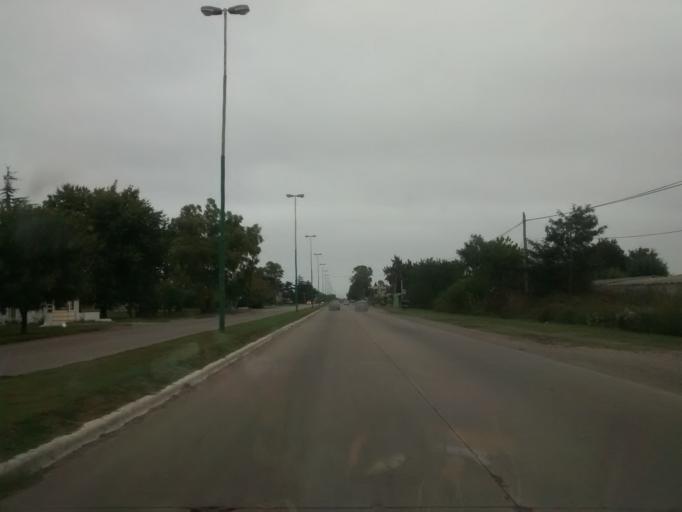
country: AR
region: Buenos Aires
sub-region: Partido de La Plata
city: La Plata
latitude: -35.0072
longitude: -58.0614
